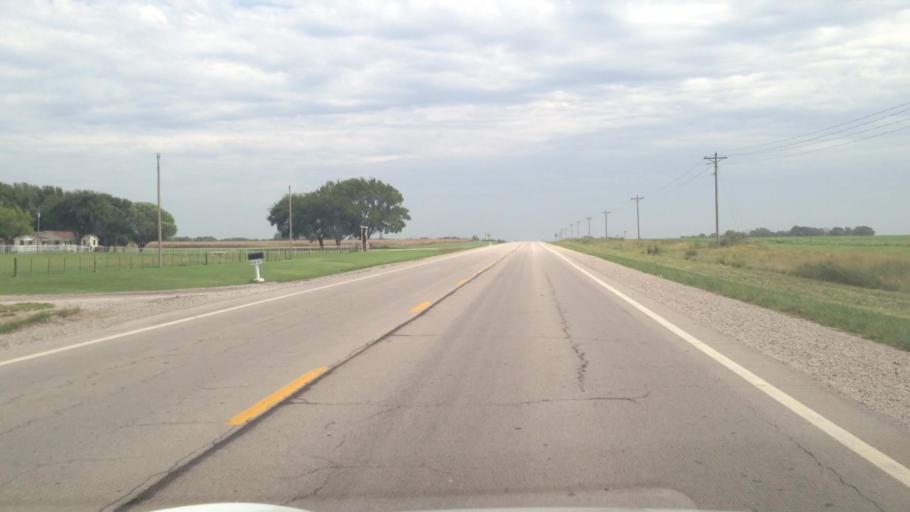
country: US
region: Kansas
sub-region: Crawford County
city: Girard
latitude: 37.5144
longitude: -94.9315
